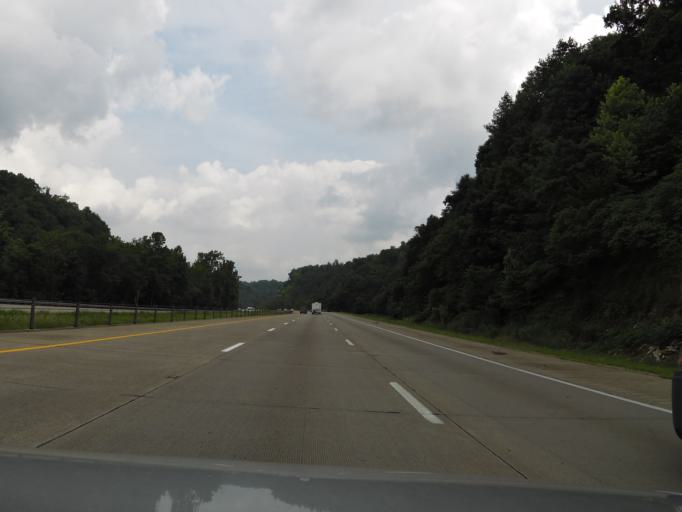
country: US
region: Kentucky
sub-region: Hardin County
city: Elizabethtown
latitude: 37.7604
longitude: -85.7955
